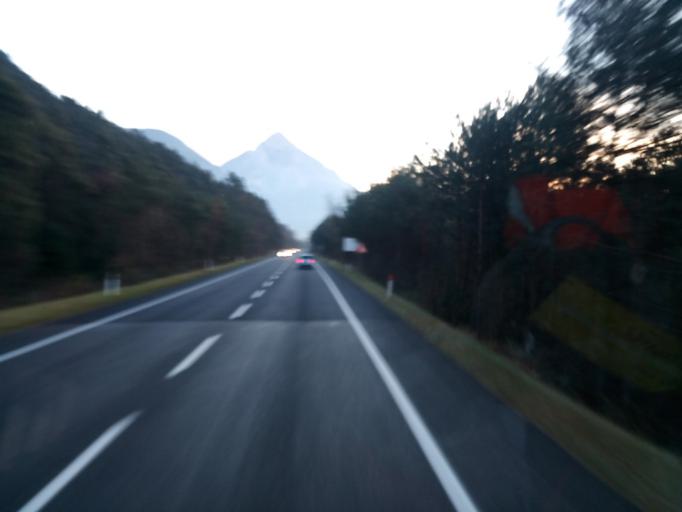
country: IT
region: Friuli Venezia Giulia
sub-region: Provincia di Udine
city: Chiaulis
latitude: 46.4072
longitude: 12.9784
